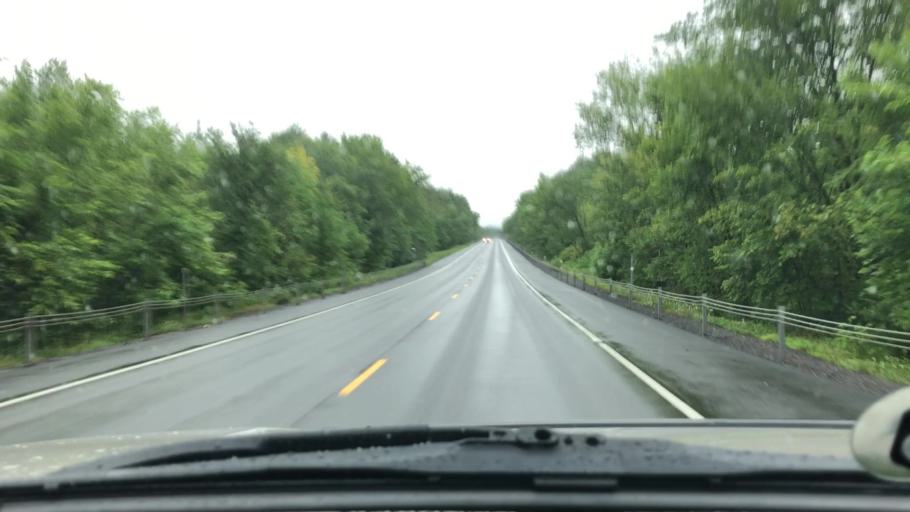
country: US
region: New York
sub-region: Greene County
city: Cairo
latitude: 42.3107
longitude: -74.0598
